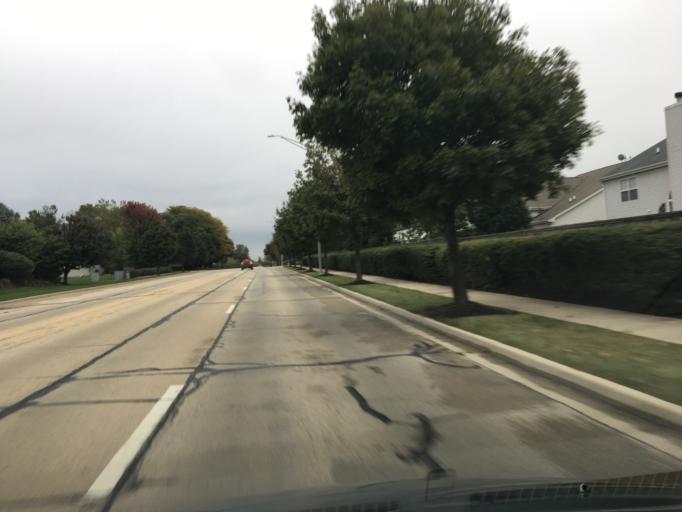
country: US
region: Illinois
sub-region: Will County
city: Plainfield
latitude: 41.6522
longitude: -88.1708
